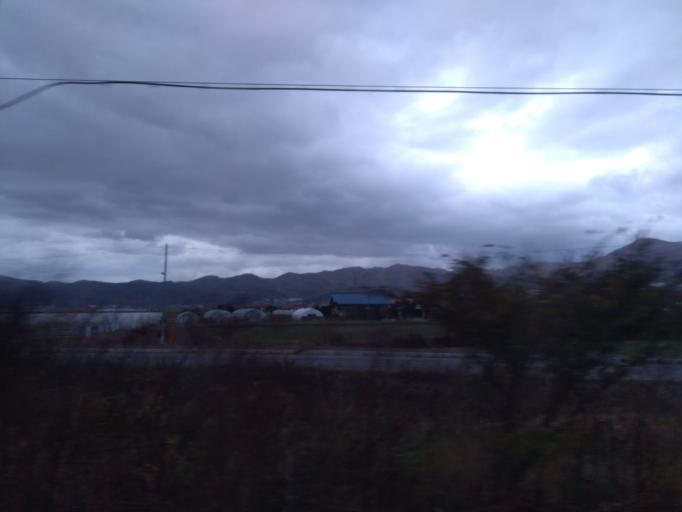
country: JP
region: Hokkaido
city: Nanae
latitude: 41.9027
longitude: 140.6598
